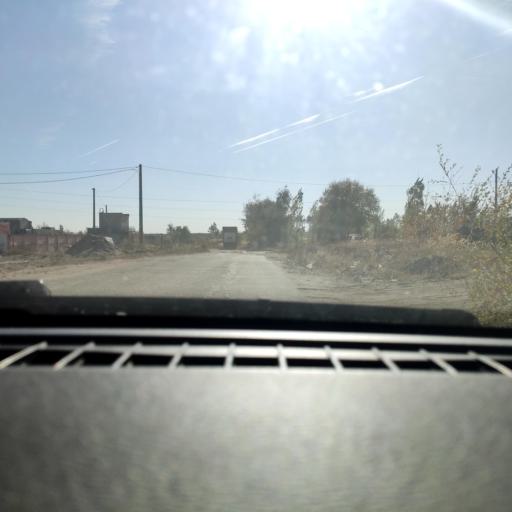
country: RU
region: Voronezj
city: Maslovka
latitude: 51.5905
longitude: 39.2369
